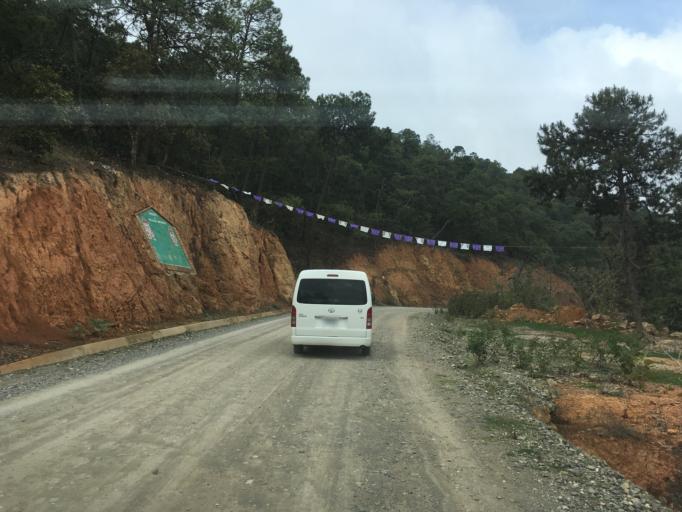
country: MX
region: Oaxaca
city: Santiago Tilantongo
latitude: 17.2060
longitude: -97.2787
